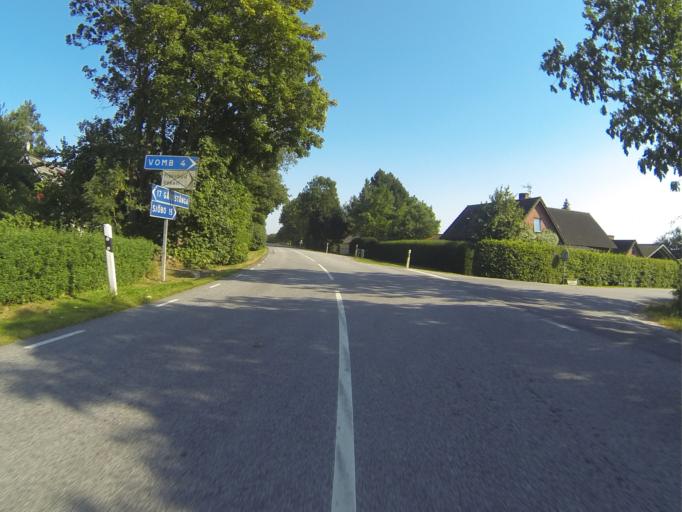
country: SE
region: Skane
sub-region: Hoors Kommun
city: Loberod
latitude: 55.7063
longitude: 13.5593
